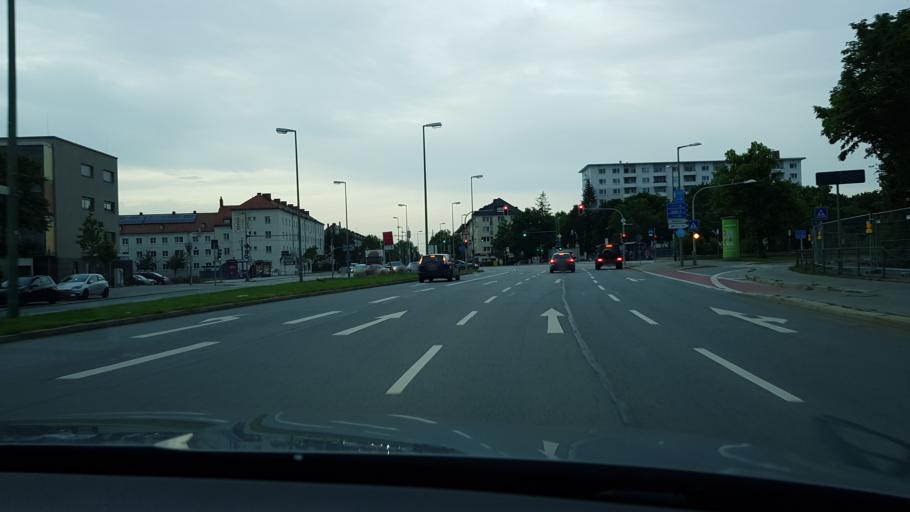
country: DE
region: Bavaria
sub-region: Upper Bavaria
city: Neuried
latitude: 48.1247
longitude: 11.5027
